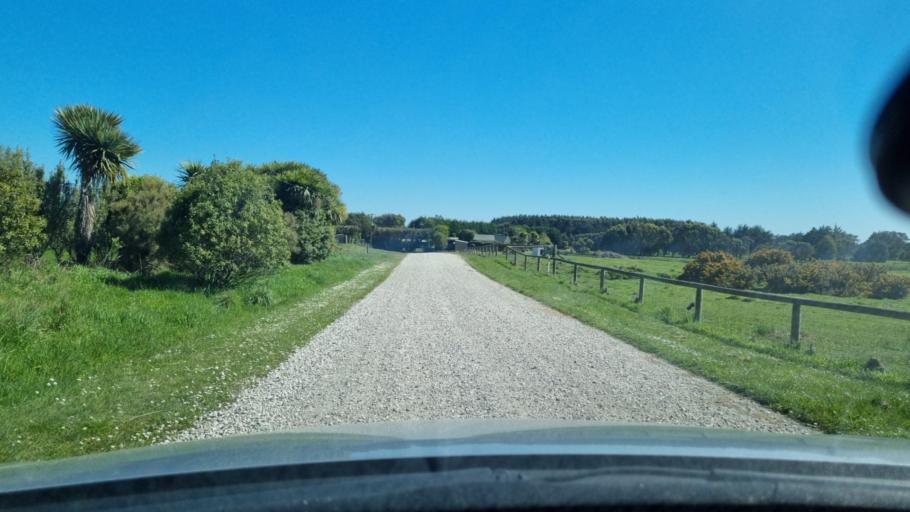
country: NZ
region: Southland
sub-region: Invercargill City
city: Invercargill
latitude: -46.4219
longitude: 168.2926
